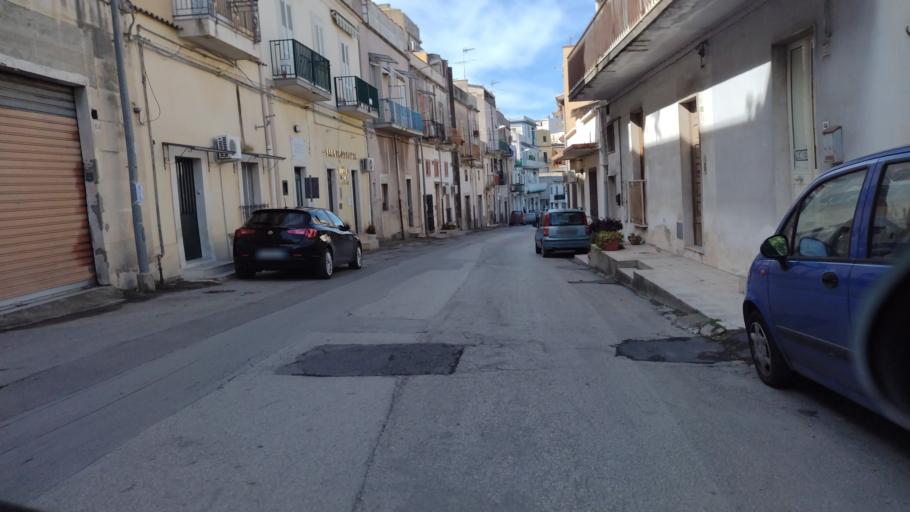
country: IT
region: Sicily
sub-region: Provincia di Siracusa
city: Noto
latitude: 36.8950
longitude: 15.0697
